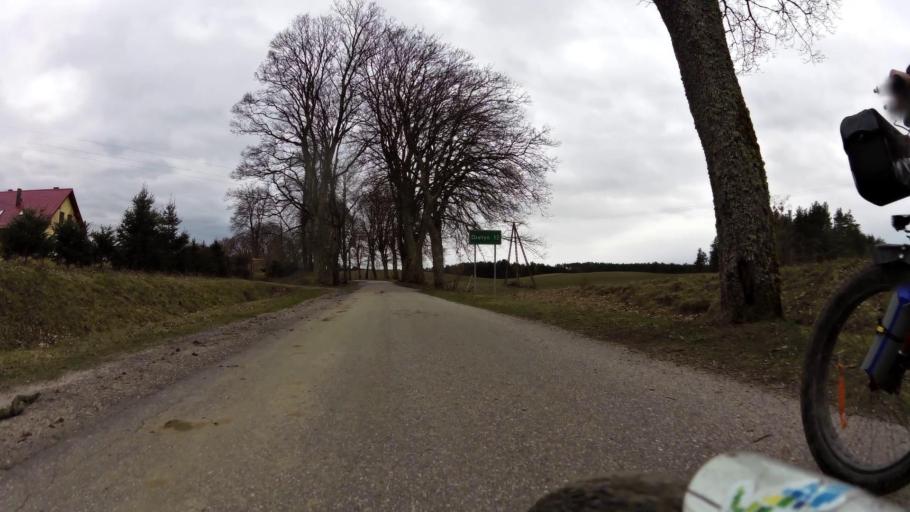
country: PL
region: Pomeranian Voivodeship
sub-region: Powiat bytowski
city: Trzebielino
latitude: 54.1042
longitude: 17.1298
